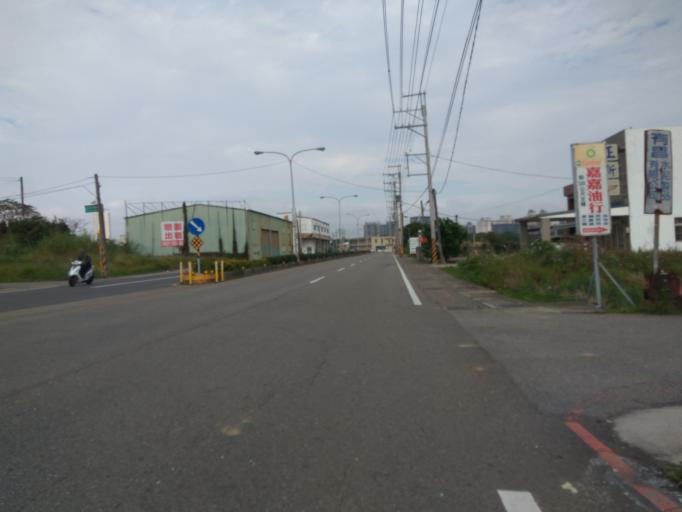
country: TW
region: Taiwan
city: Taoyuan City
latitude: 24.9975
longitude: 121.2190
